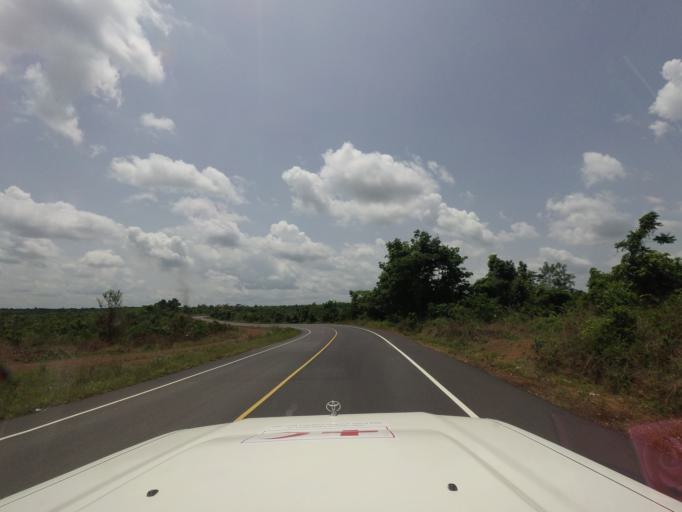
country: LR
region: Margibi
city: Kakata
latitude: 6.5047
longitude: -10.3914
